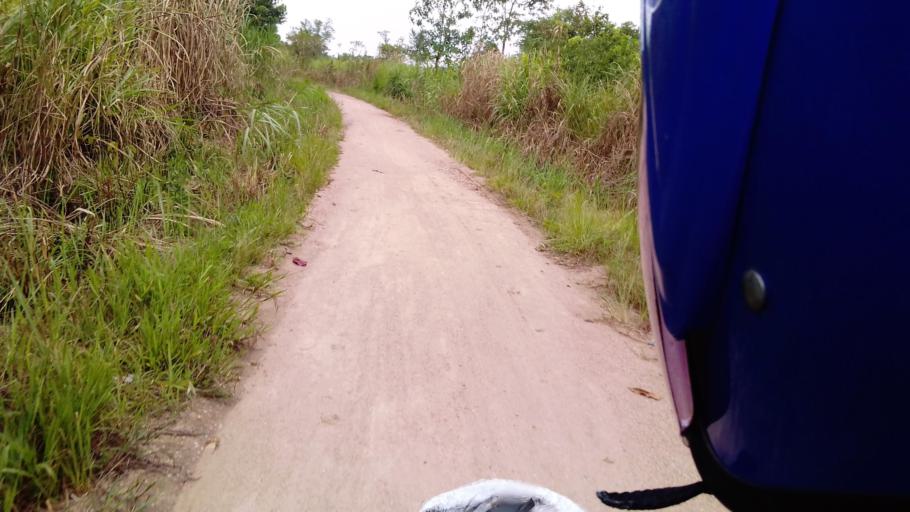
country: SL
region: Eastern Province
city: Koidu
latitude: 8.6754
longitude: -10.9858
